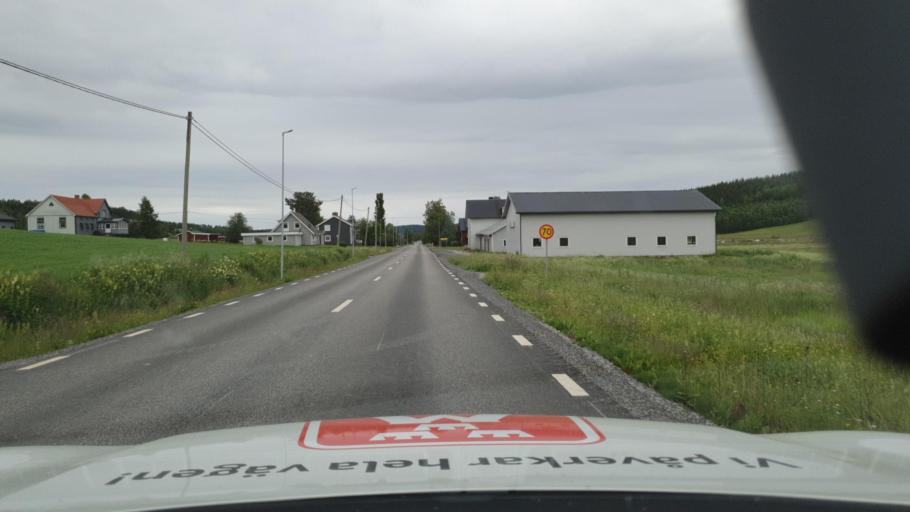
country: SE
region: Vaesterbotten
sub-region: Vannas Kommun
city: Vaennaes
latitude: 63.7616
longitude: 19.6290
